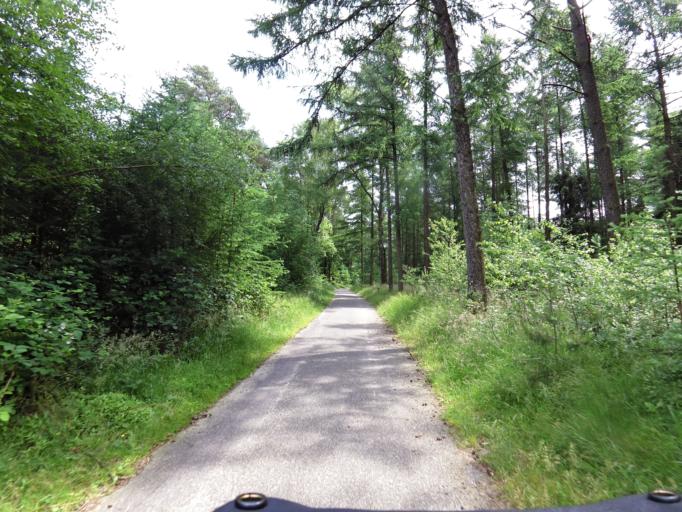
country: NL
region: Gelderland
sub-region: Gemeente Rozendaal
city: Rozendaal
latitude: 52.0232
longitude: 5.9838
